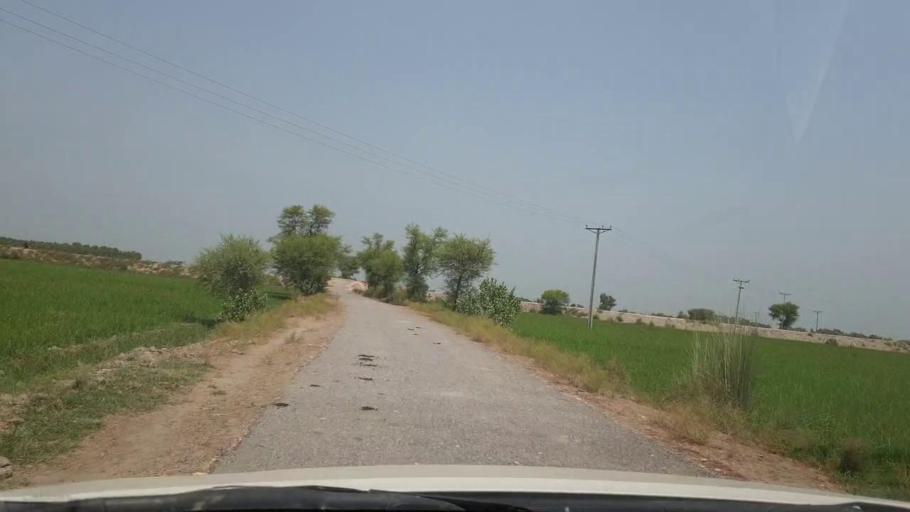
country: PK
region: Sindh
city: Rustam jo Goth
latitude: 28.0212
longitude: 68.7867
